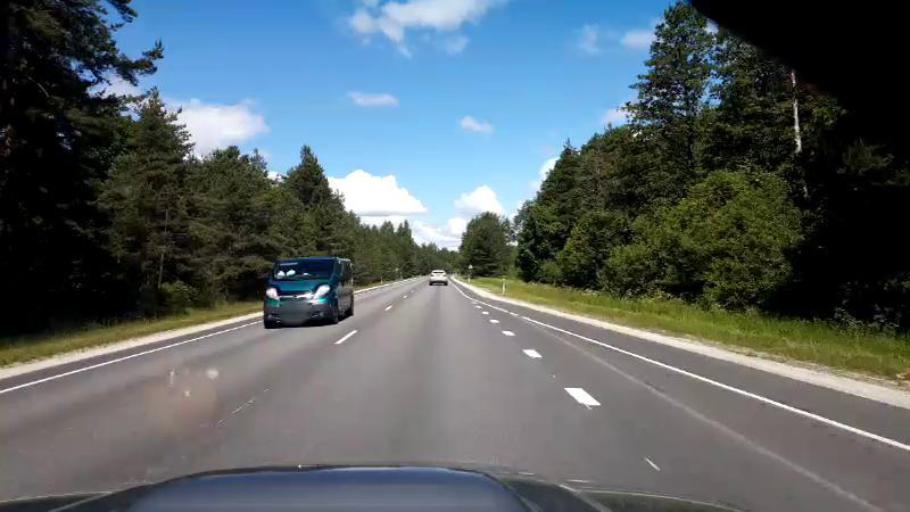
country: EE
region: Paernumaa
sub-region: Paernu linn
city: Parnu
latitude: 58.2146
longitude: 24.4866
